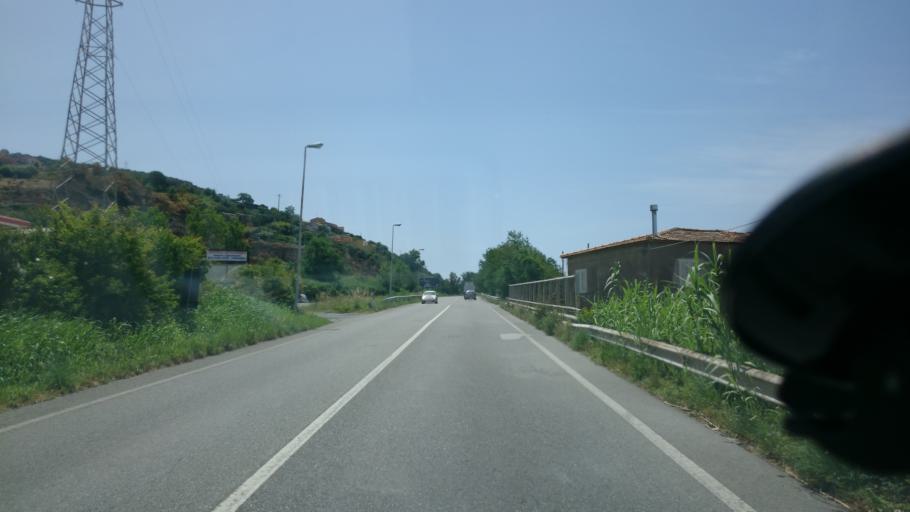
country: IT
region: Calabria
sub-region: Provincia di Cosenza
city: Cittadella del Capo
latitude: 39.5599
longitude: 15.8768
